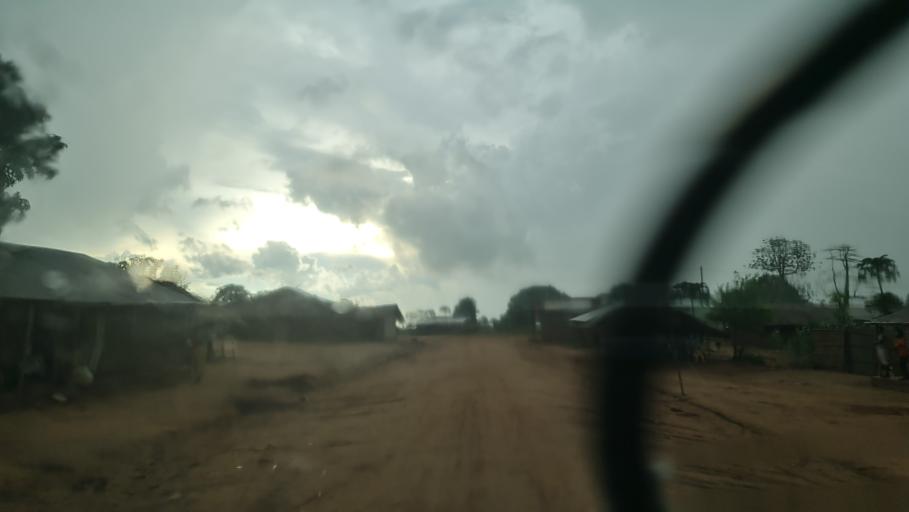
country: MZ
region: Nampula
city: Nacala
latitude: -14.0042
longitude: 40.3498
